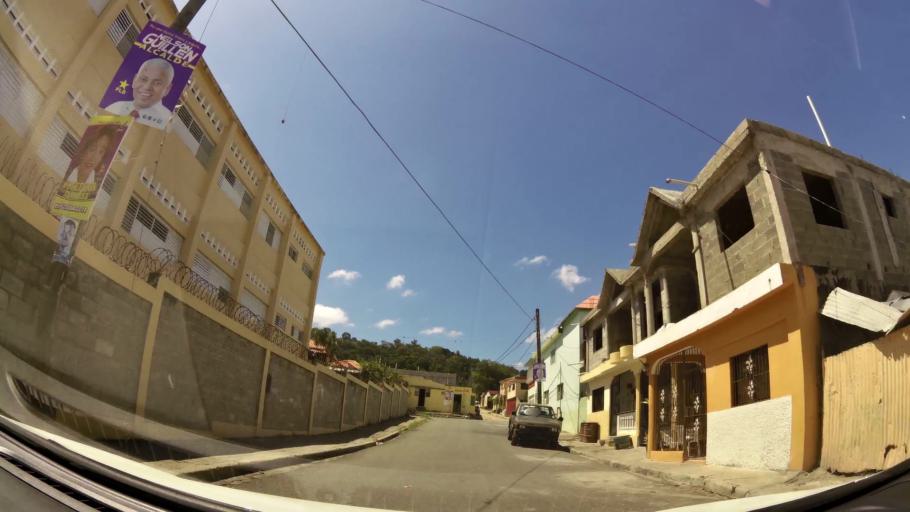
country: DO
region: San Cristobal
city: San Cristobal
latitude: 18.4055
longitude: -70.1131
